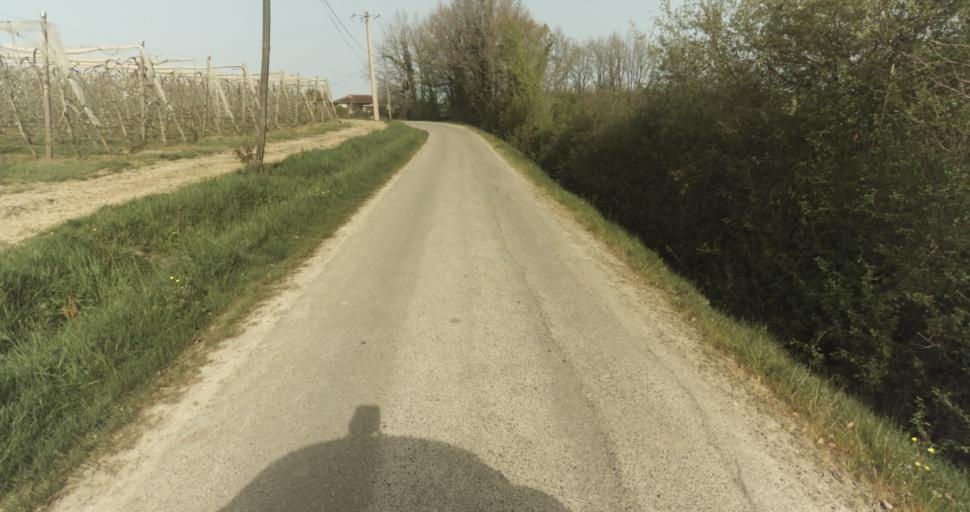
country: FR
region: Midi-Pyrenees
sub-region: Departement du Tarn-et-Garonne
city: Moissac
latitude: 44.1520
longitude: 1.0690
